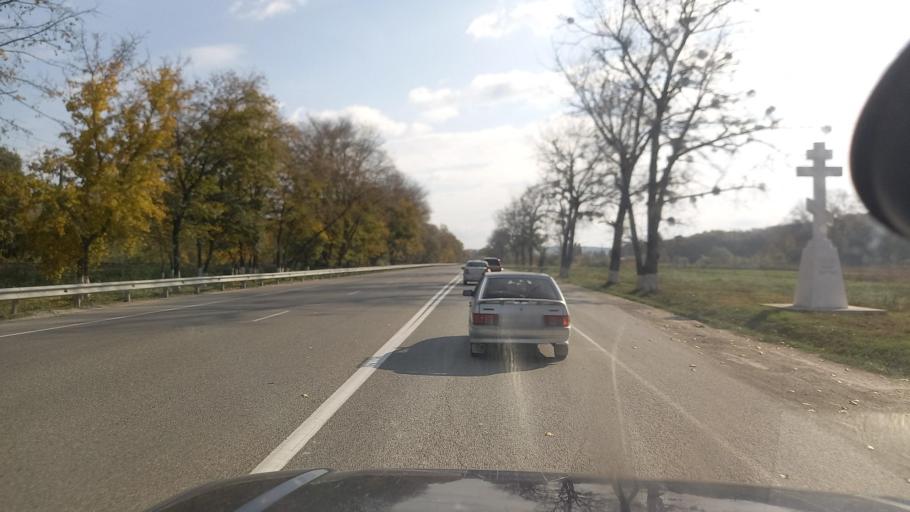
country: RU
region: Krasnodarskiy
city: Gayduk
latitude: 44.8728
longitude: 37.8306
